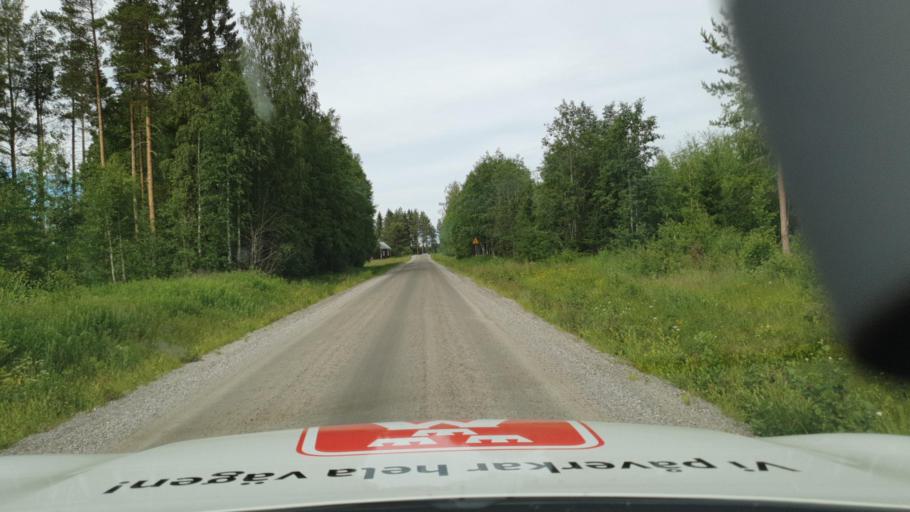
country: SE
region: Vaesterbotten
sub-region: Skelleftea Kommun
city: Viken
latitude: 64.5062
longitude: 20.9293
